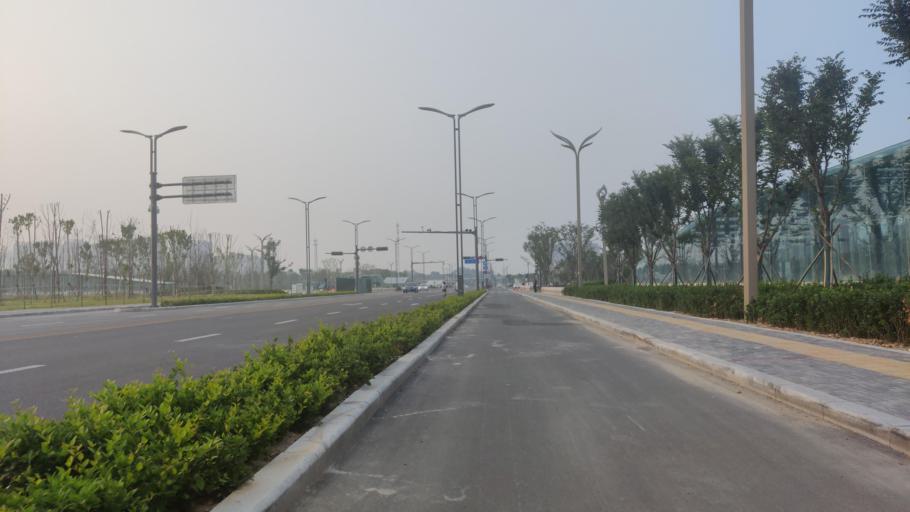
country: CN
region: Henan Sheng
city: Zhongyuanlu
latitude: 35.7633
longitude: 115.1413
